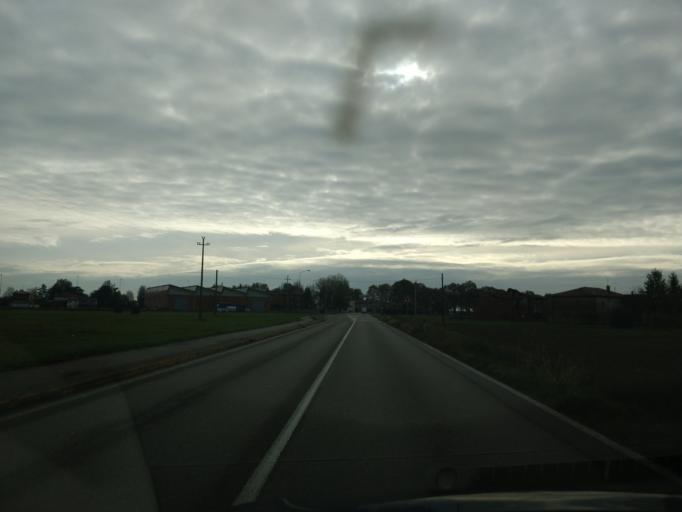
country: IT
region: Emilia-Romagna
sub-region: Provincia di Bologna
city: Castello d'Argile
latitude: 44.6695
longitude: 11.3035
